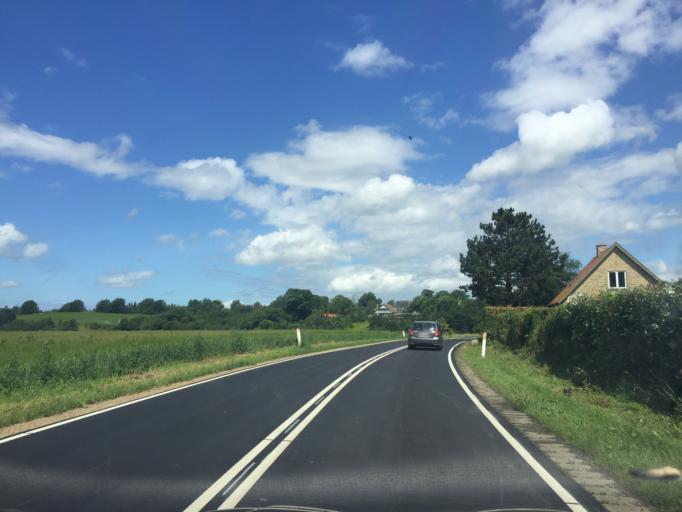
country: DK
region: Capital Region
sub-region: Allerod Kommune
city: Lynge
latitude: 55.8290
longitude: 12.2729
